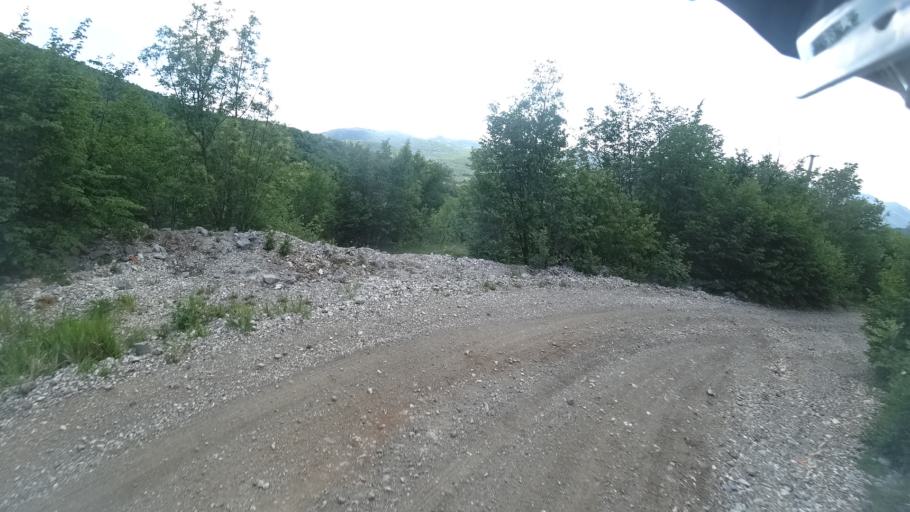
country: HR
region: Zadarska
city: Gracac
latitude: 44.2812
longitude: 15.9370
